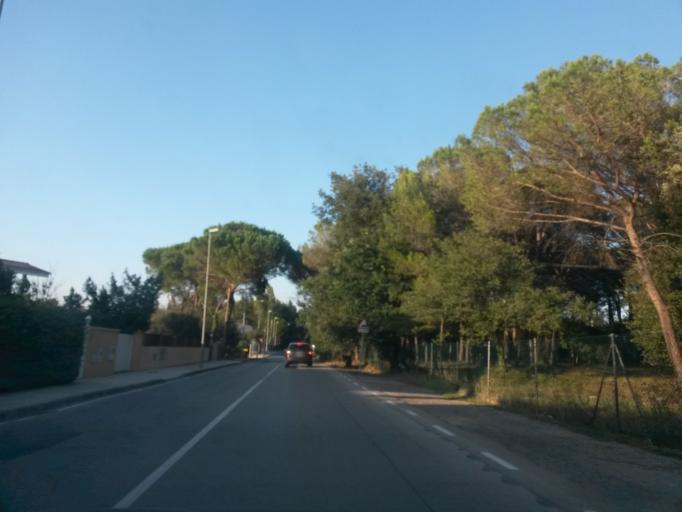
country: ES
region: Catalonia
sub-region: Provincia de Girona
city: Fornells de la Selva
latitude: 41.9417
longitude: 2.8092
